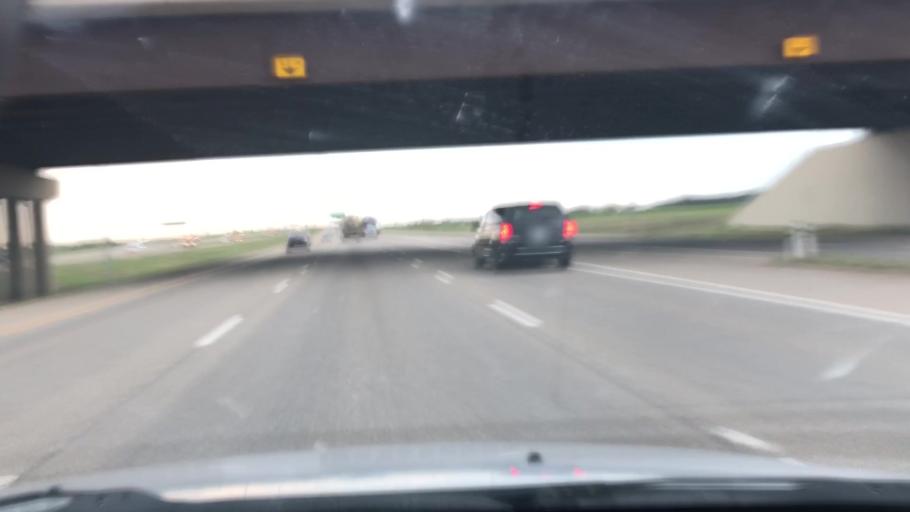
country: CA
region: Alberta
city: Beaumont
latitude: 53.4376
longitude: -113.4662
